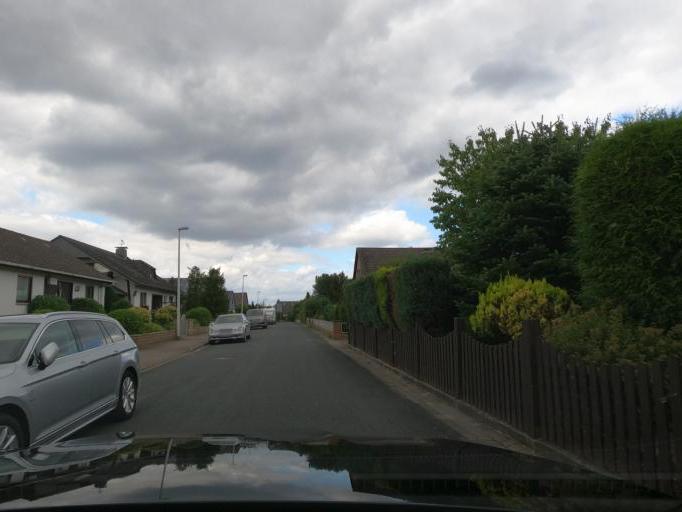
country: DE
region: Lower Saxony
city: Lehrte
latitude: 52.3727
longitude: 9.9044
